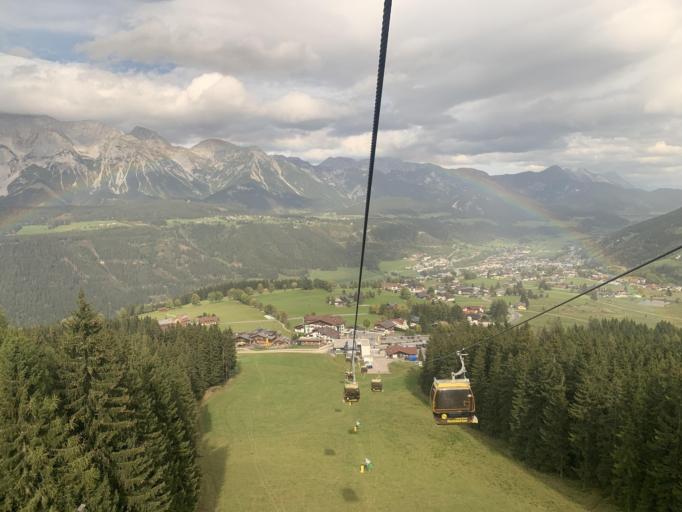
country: AT
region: Styria
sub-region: Politischer Bezirk Liezen
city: Schladming
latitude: 47.3733
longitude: 13.6513
